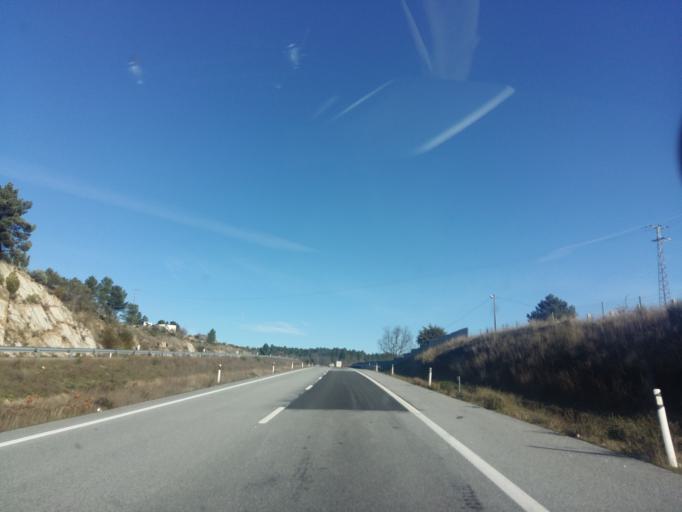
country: PT
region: Guarda
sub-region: Guarda
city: Sequeira
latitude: 40.5780
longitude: -7.1809
